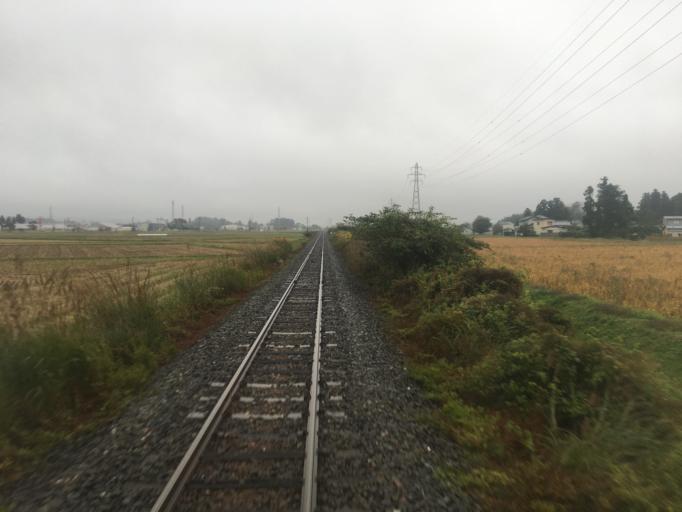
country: JP
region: Miyagi
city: Kogota
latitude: 38.5573
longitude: 141.0335
